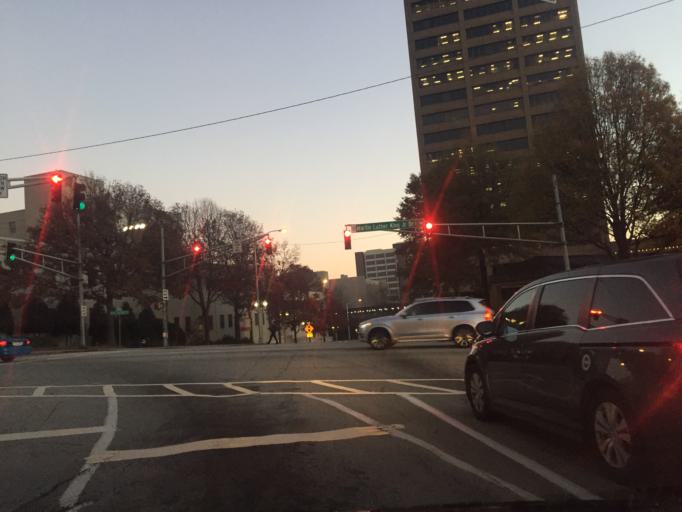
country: US
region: Georgia
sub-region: Fulton County
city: Atlanta
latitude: 33.7492
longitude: -84.3874
